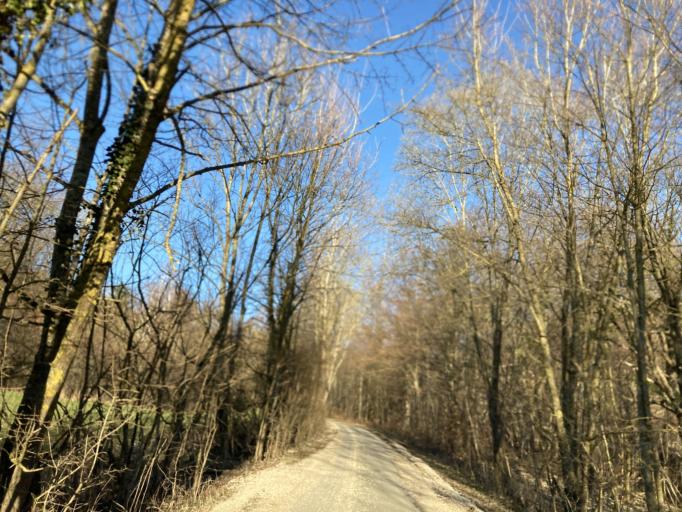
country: DE
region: Baden-Wuerttemberg
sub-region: Tuebingen Region
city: Nehren
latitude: 48.3929
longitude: 9.1119
